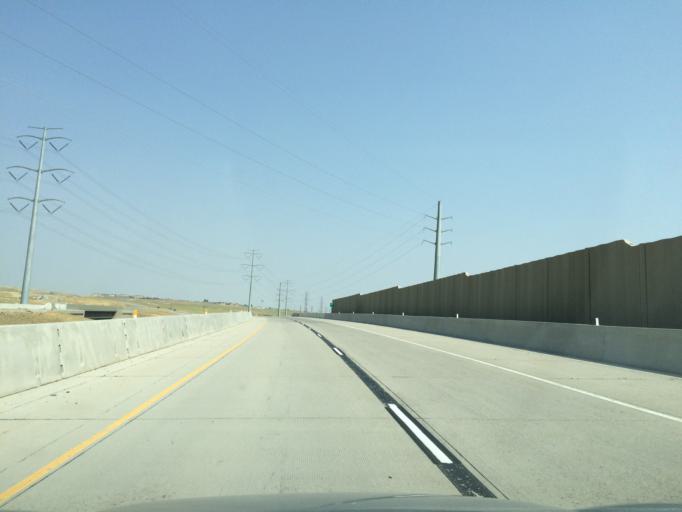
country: US
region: Utah
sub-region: Salt Lake County
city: Oquirrh
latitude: 40.6009
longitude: -112.0292
